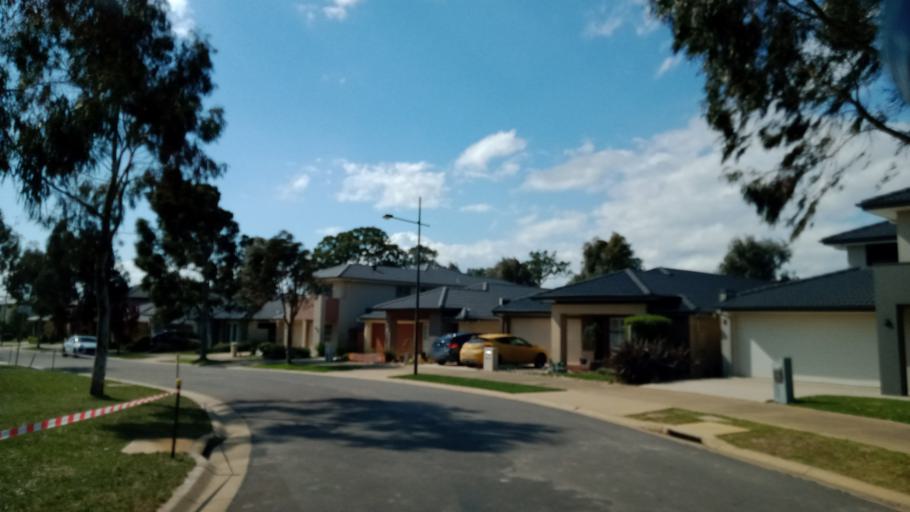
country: AU
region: Victoria
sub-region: Frankston
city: Sandhurst
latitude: -38.0834
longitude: 145.2114
